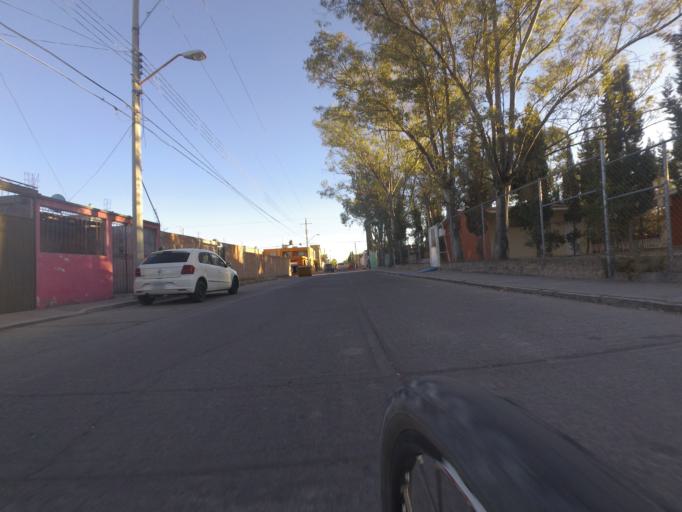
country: MX
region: Aguascalientes
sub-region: Aguascalientes
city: La Loma de los Negritos
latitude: 21.8522
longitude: -102.3402
